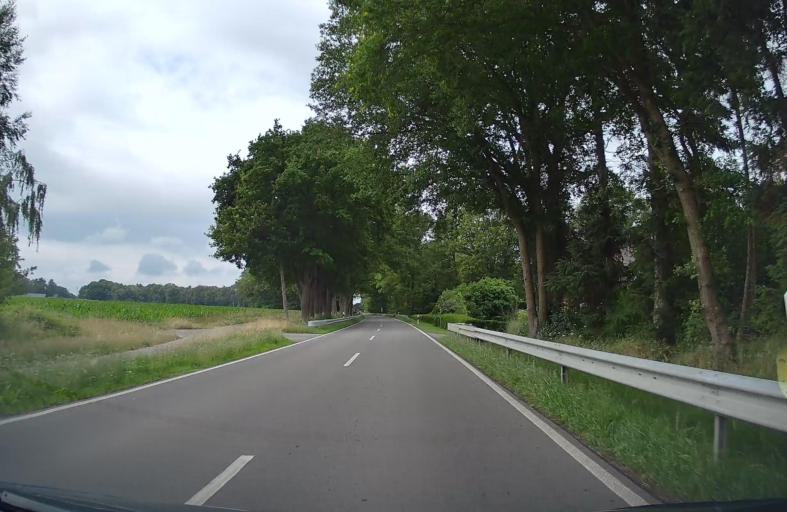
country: DE
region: Lower Saxony
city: Friesoythe
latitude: 53.0417
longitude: 7.8316
